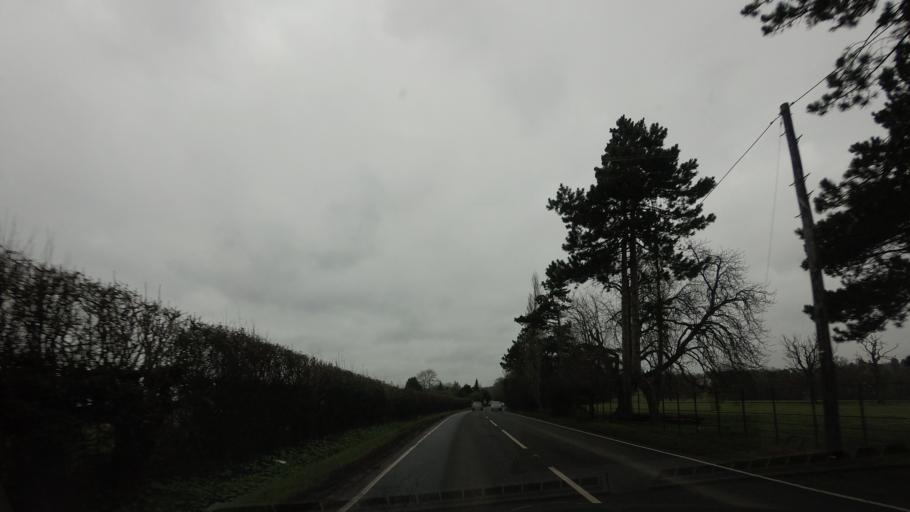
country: GB
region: England
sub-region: Kent
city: Marden
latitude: 51.2133
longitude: 0.5136
